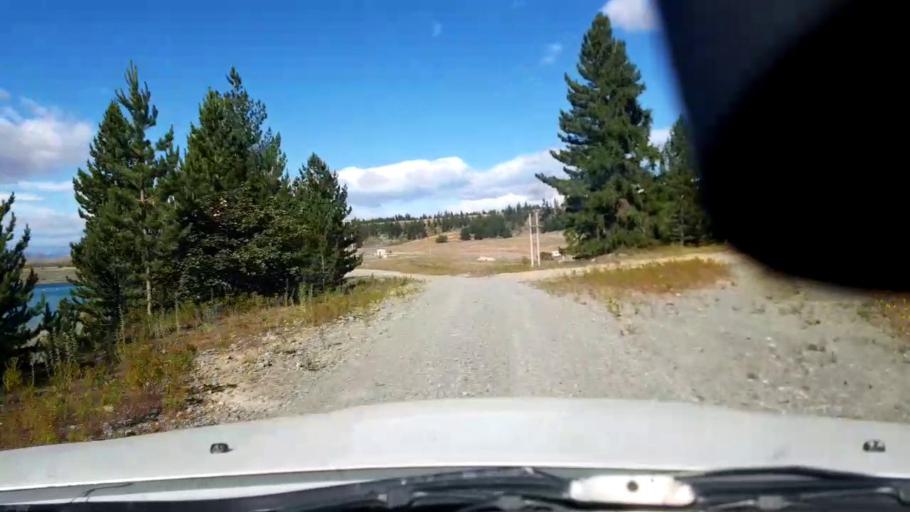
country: NZ
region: Canterbury
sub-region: Timaru District
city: Pleasant Point
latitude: -44.0132
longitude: 170.4647
